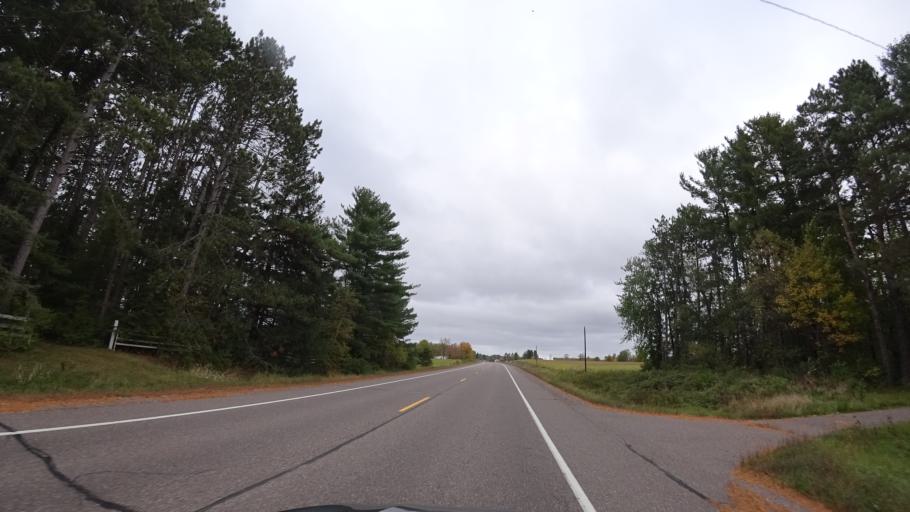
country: US
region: Wisconsin
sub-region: Rusk County
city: Ladysmith
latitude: 45.5420
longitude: -91.1114
